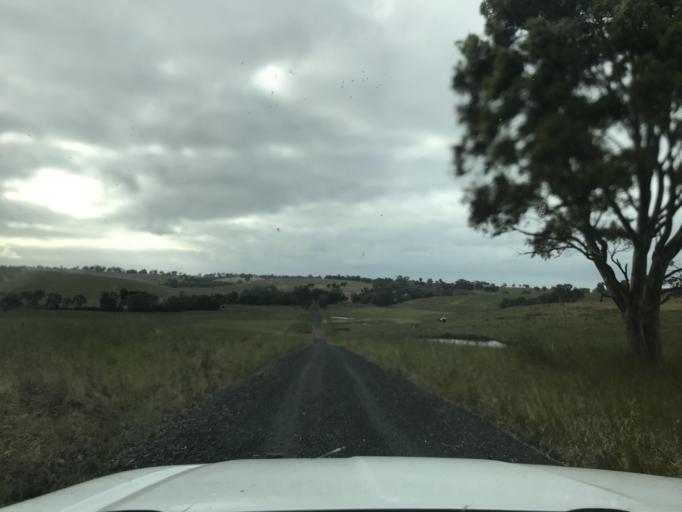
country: AU
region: South Australia
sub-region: Wattle Range
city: Penola
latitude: -37.2803
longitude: 141.4008
